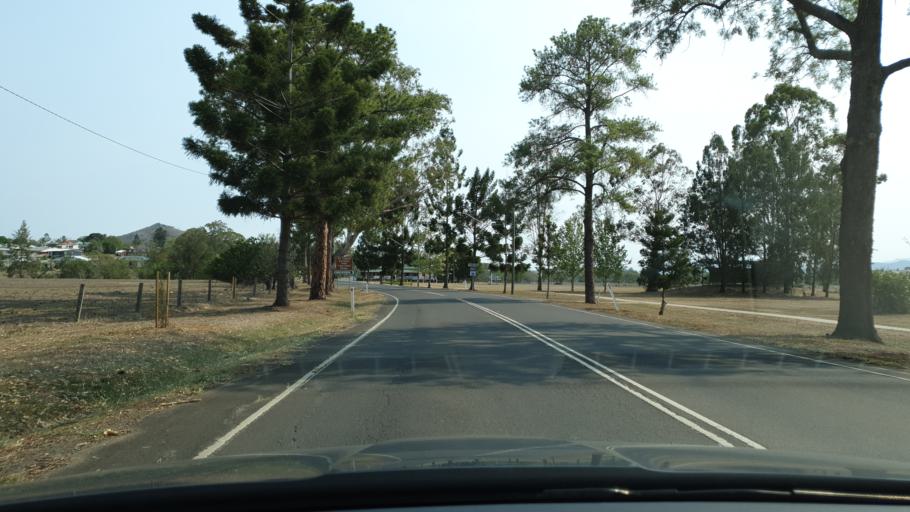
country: AU
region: Queensland
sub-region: Ipswich
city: Deebing Heights
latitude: -28.0021
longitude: 152.6815
